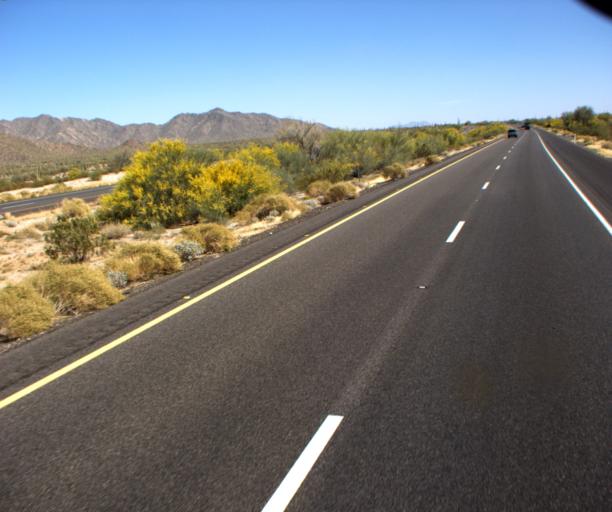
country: US
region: Arizona
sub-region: Maricopa County
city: Gila Bend
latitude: 32.8762
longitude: -112.4481
